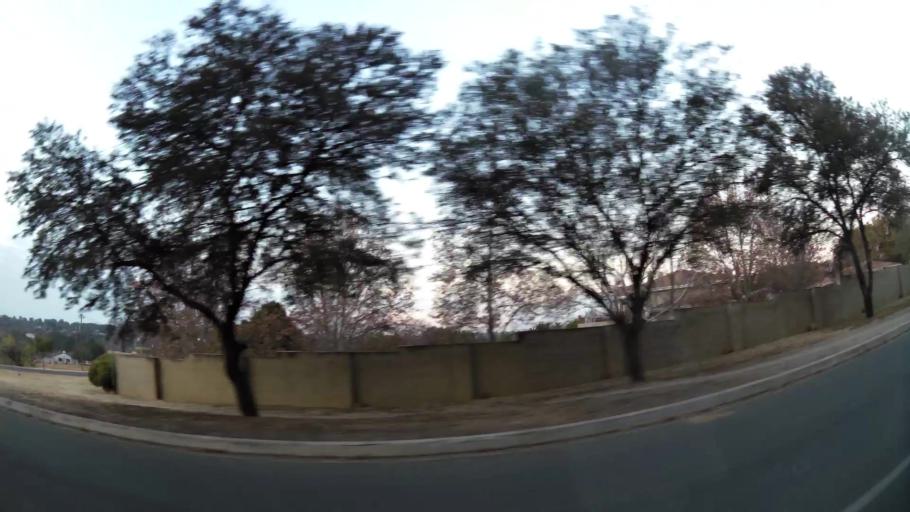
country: ZA
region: Gauteng
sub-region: City of Johannesburg Metropolitan Municipality
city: Midrand
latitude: -25.9827
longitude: 28.0649
